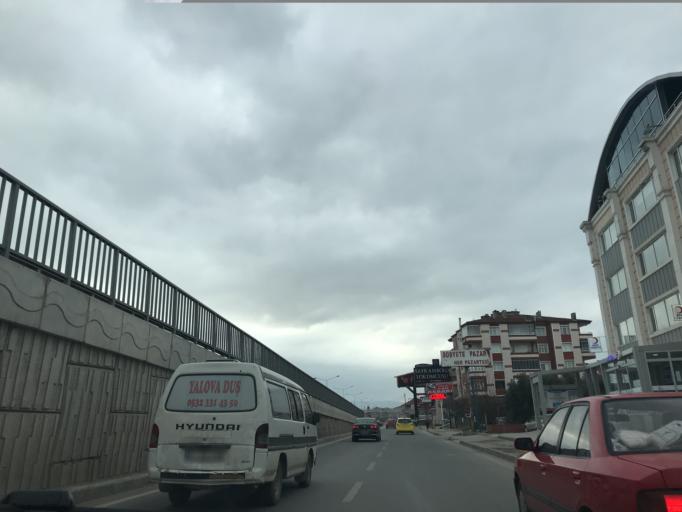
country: TR
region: Yalova
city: Ciftlikkoy
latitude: 40.6641
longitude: 29.3207
